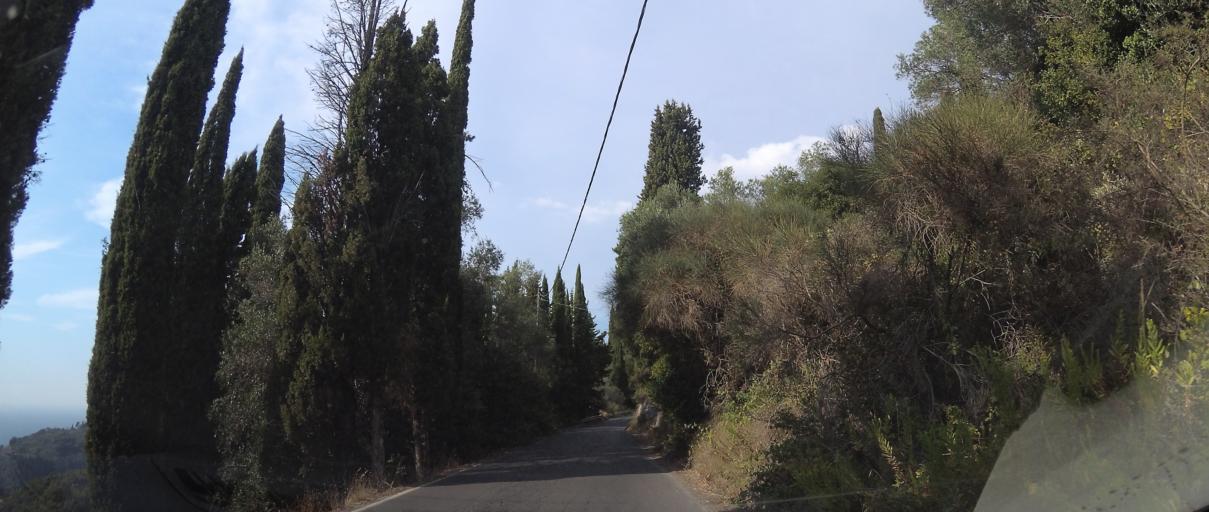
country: GR
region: Ionian Islands
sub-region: Nomos Kerkyras
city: Kynopiastes
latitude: 39.5505
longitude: 19.8634
